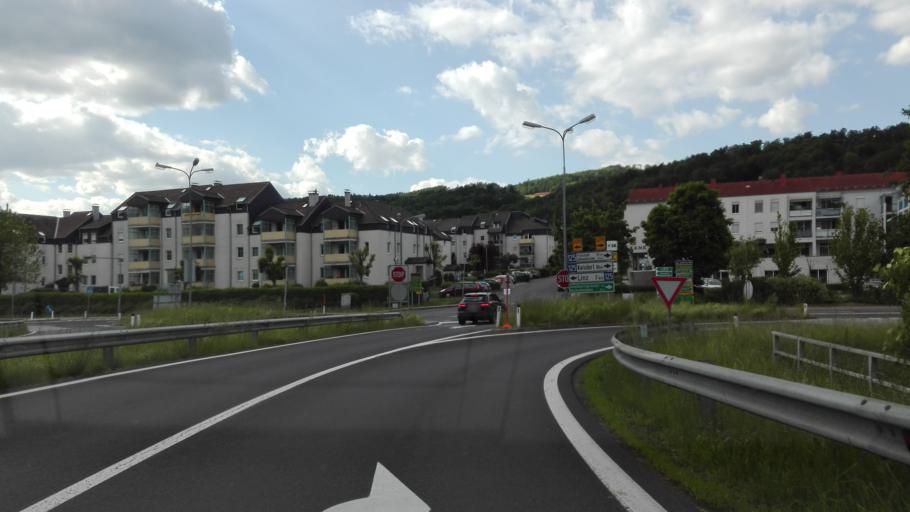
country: AT
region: Upper Austria
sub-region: Politischer Bezirk Urfahr-Umgebung
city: Altenberg bei Linz
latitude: 48.3365
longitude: 14.3654
